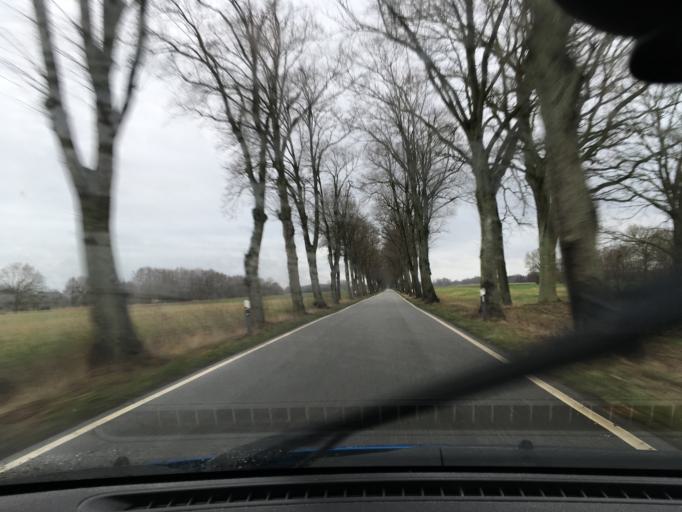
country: DE
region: Lower Saxony
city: Hittbergen
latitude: 53.3585
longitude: 10.6084
